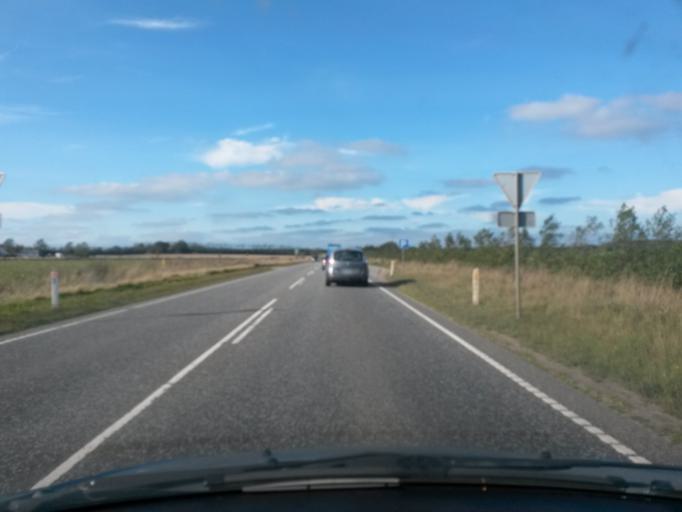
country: DK
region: Central Jutland
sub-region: Herning Kommune
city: Avlum
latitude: 56.2669
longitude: 8.7715
